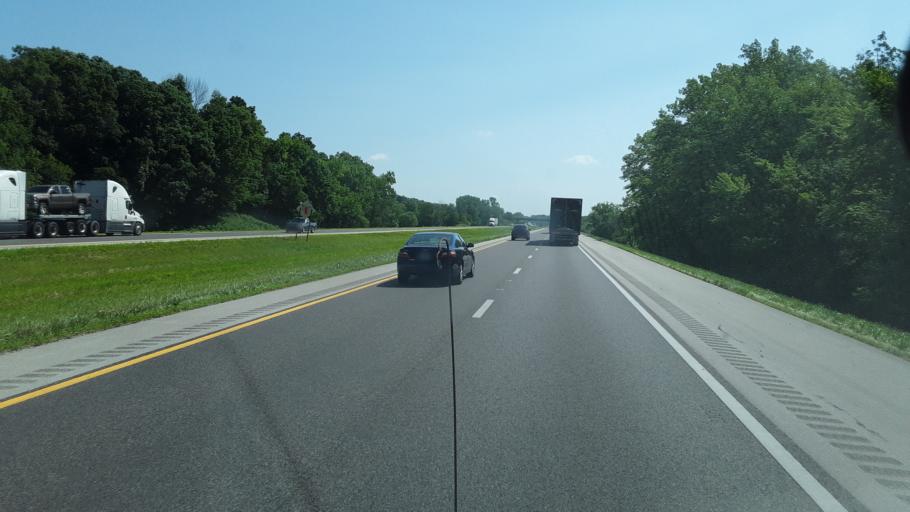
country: US
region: Illinois
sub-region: Cumberland County
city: Toledo
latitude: 39.2100
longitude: -88.2685
